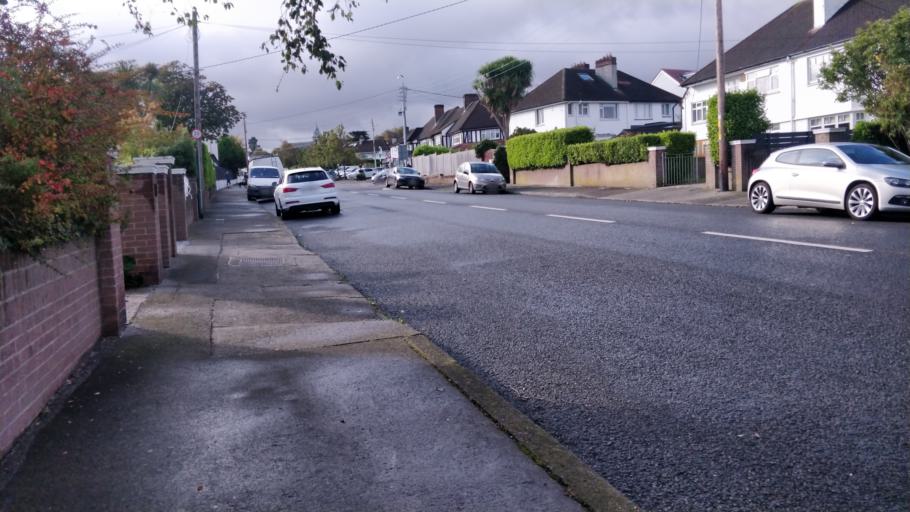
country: IE
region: Leinster
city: Mount Merrion
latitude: 53.3003
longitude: -6.2084
